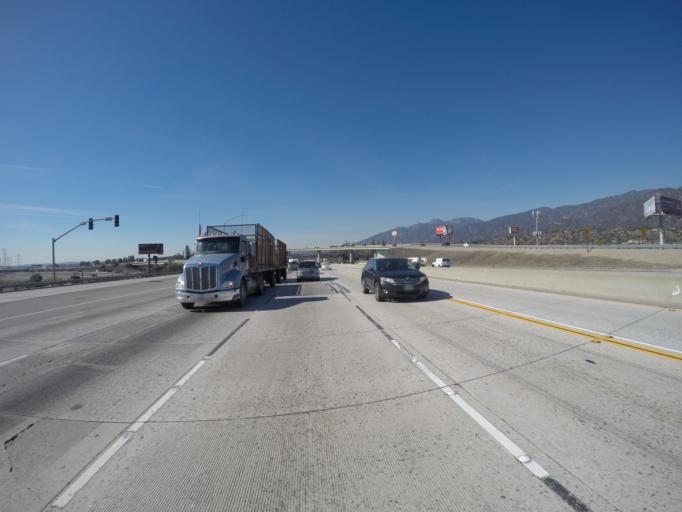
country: US
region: California
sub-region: Los Angeles County
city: Bradbury
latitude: 34.1334
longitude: -117.9540
